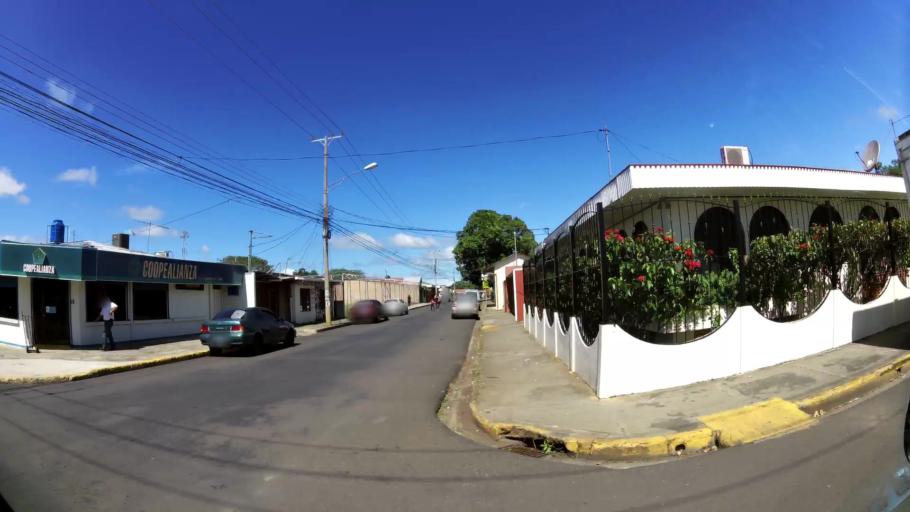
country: CR
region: Guanacaste
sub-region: Canton de Canas
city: Canas
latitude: 10.4281
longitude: -85.0903
